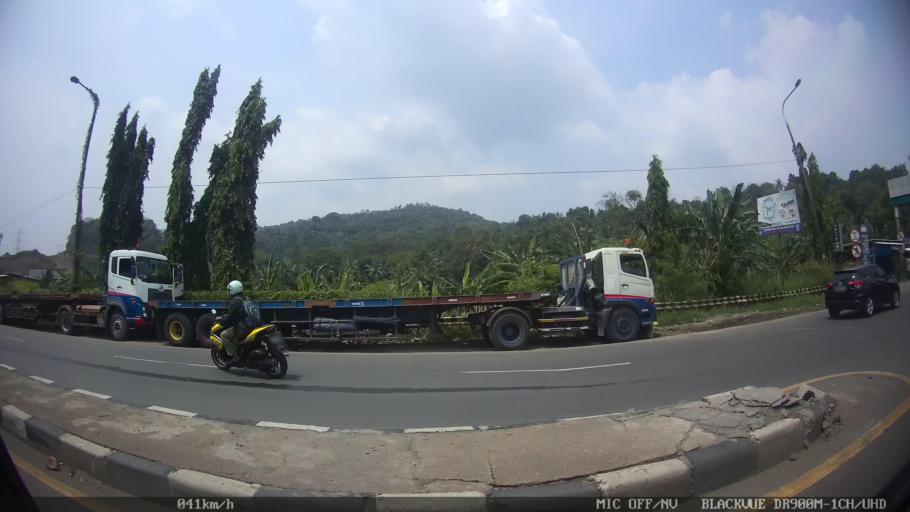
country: ID
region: Banten
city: Curug
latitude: -5.9709
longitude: 106.0074
